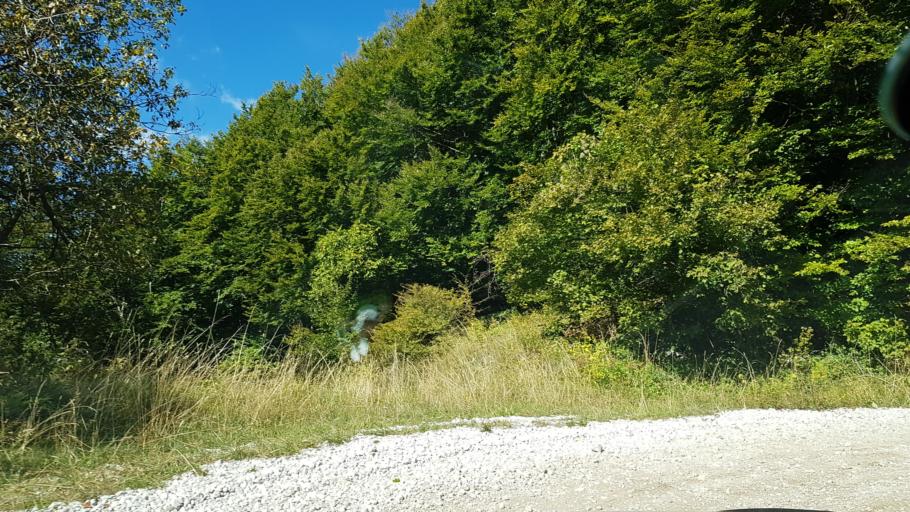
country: SI
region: Kobarid
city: Kobarid
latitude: 46.2783
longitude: 13.6187
